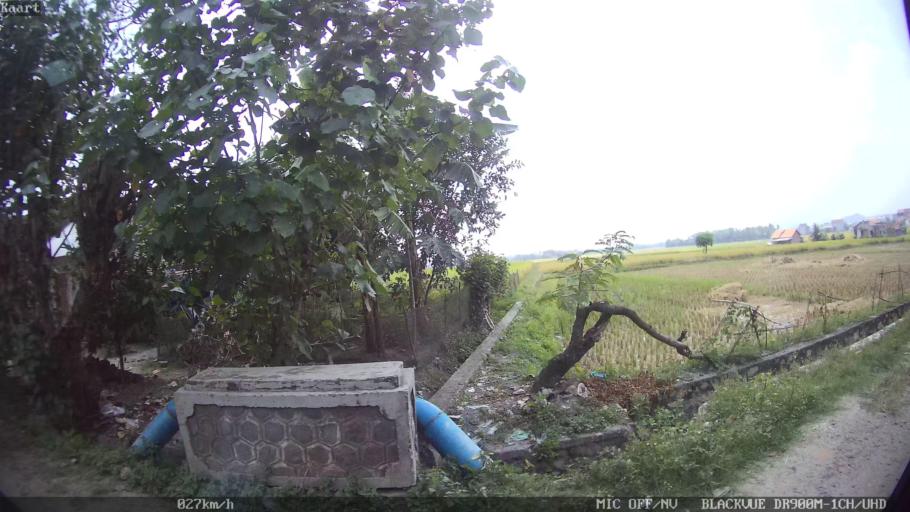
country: ID
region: Lampung
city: Pringsewu
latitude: -5.3500
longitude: 104.9904
